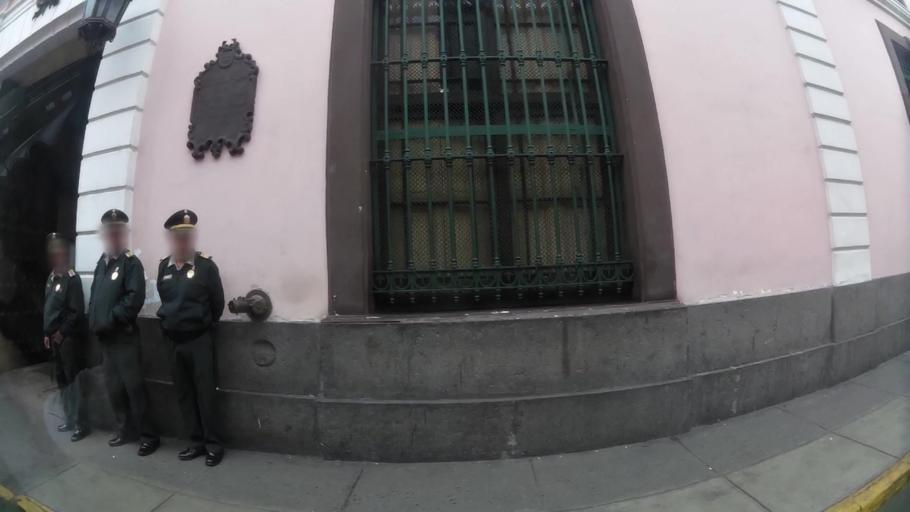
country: PE
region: Lima
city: Lima
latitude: -12.0494
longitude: -77.0240
